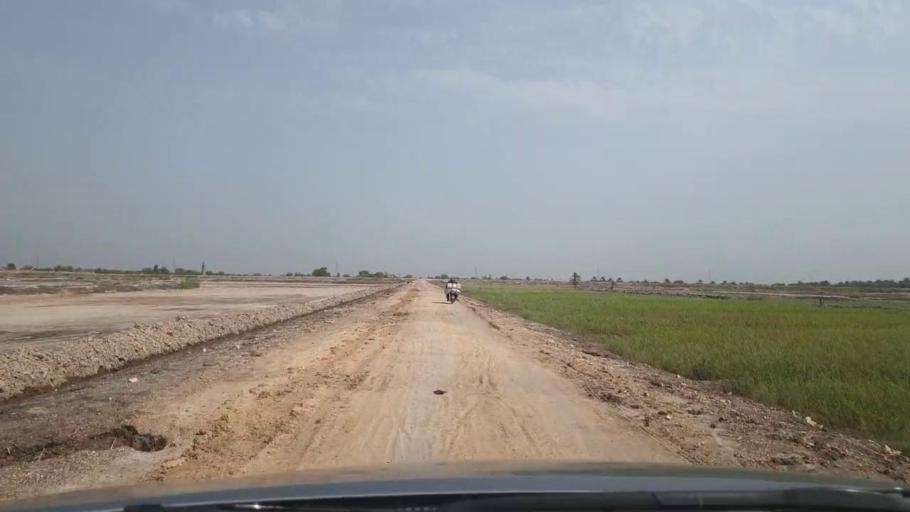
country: PK
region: Sindh
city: Rohri
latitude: 27.6757
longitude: 69.0260
